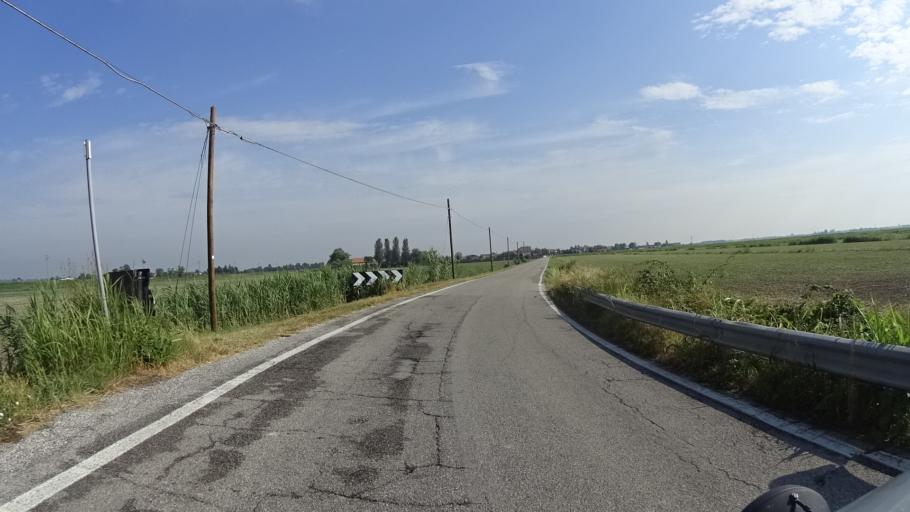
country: IT
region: Veneto
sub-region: Provincia di Venezia
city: Lugugnana
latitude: 45.6973
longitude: 12.9478
